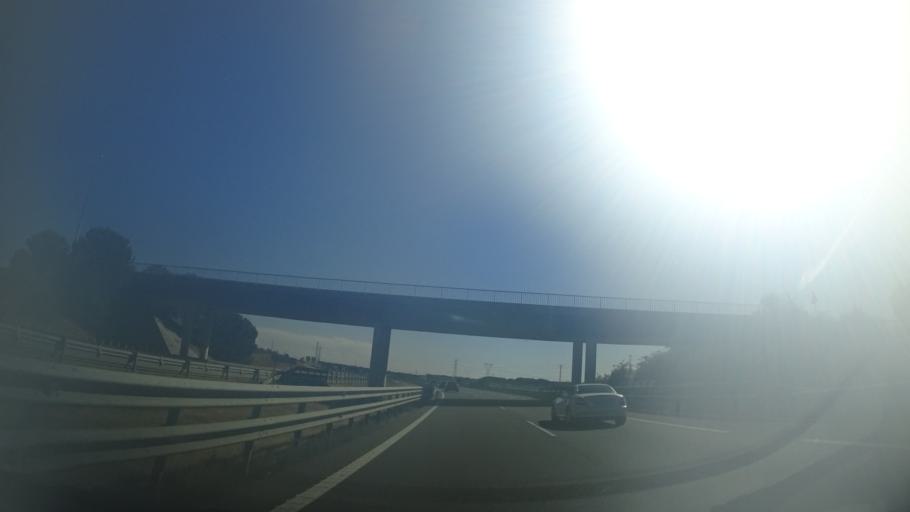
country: ES
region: Castille and Leon
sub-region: Provincia de Valladolid
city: Tordesillas
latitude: 41.4812
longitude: -4.9905
